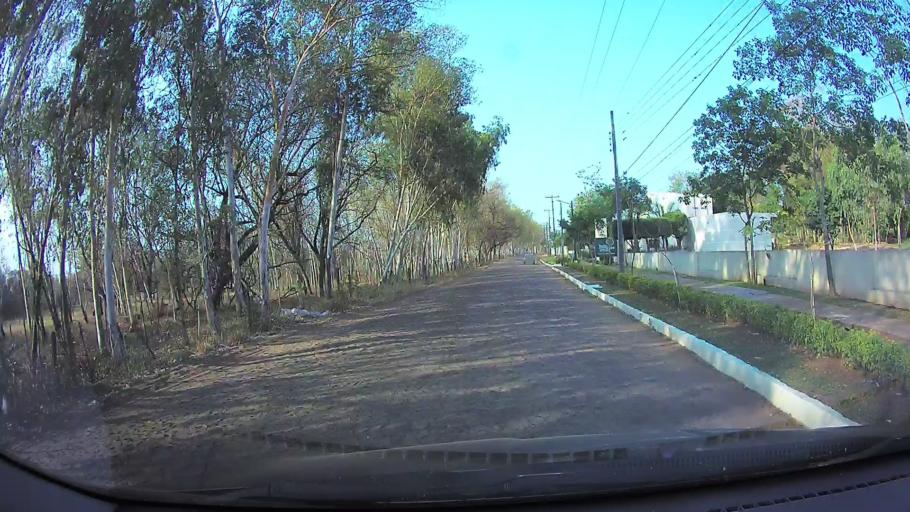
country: PY
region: Central
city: Limpio
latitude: -25.2245
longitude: -57.5072
